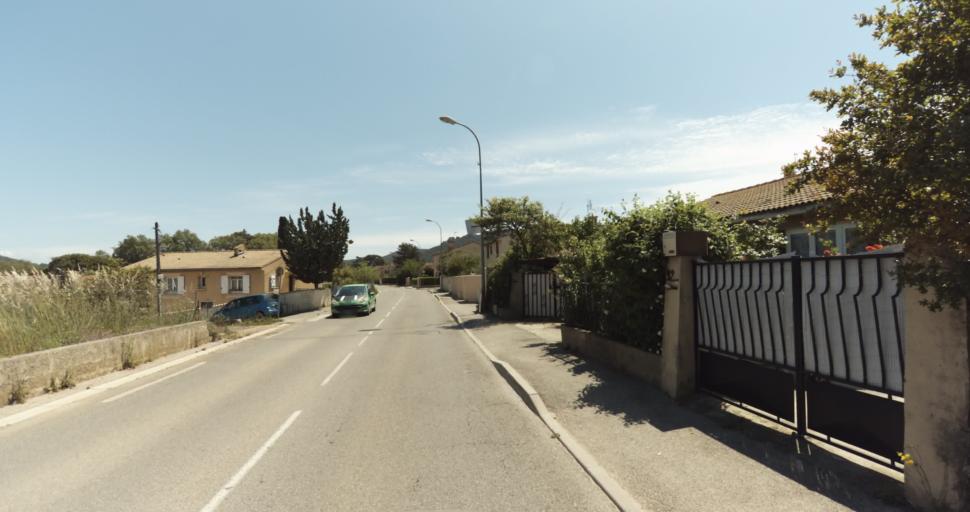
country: FR
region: Provence-Alpes-Cote d'Azur
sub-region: Departement du Var
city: La Crau
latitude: 43.1497
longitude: 6.0793
